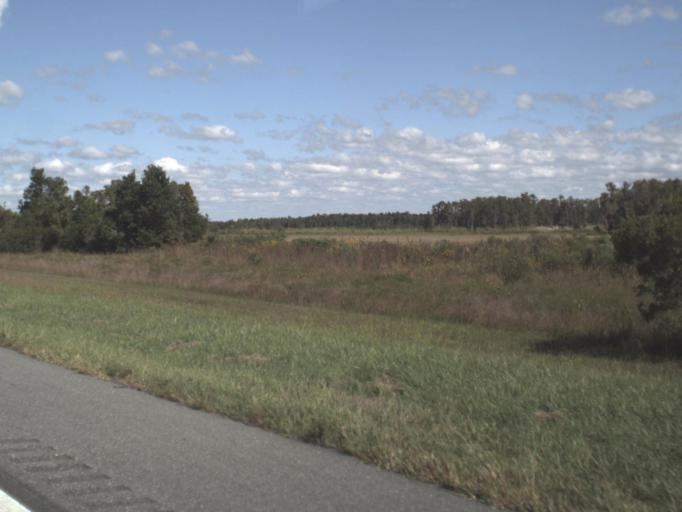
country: US
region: Florida
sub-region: Osceola County
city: Saint Cloud
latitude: 28.1236
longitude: -81.2866
